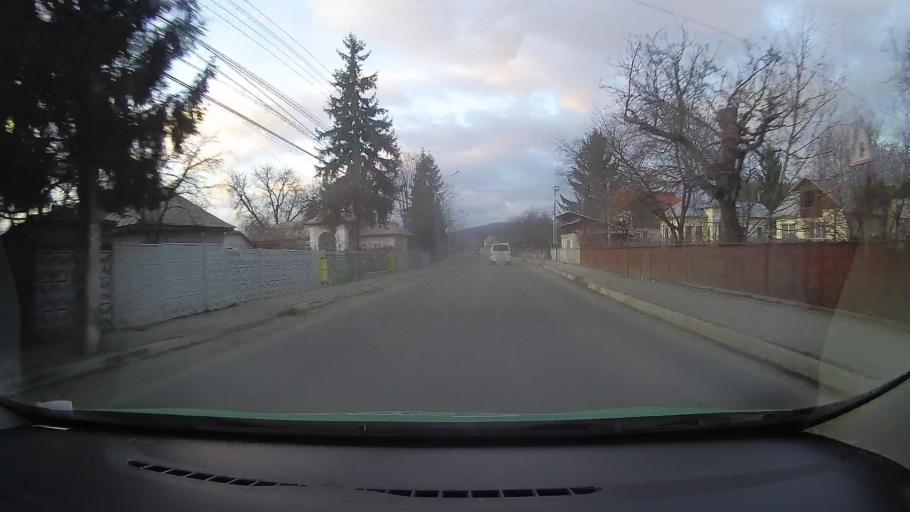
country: RO
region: Dambovita
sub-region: Municipiul Moreni
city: Moreni
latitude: 44.9961
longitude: 25.6482
